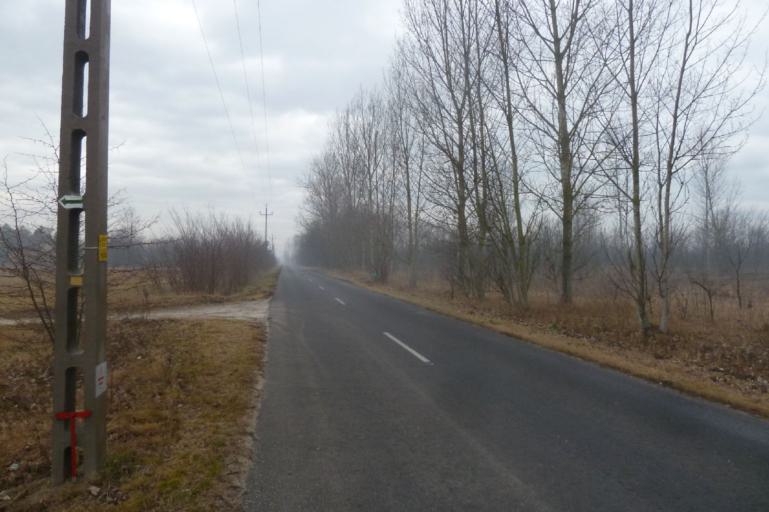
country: HU
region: Pest
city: Tapioszentmarton
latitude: 47.3519
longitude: 19.7886
